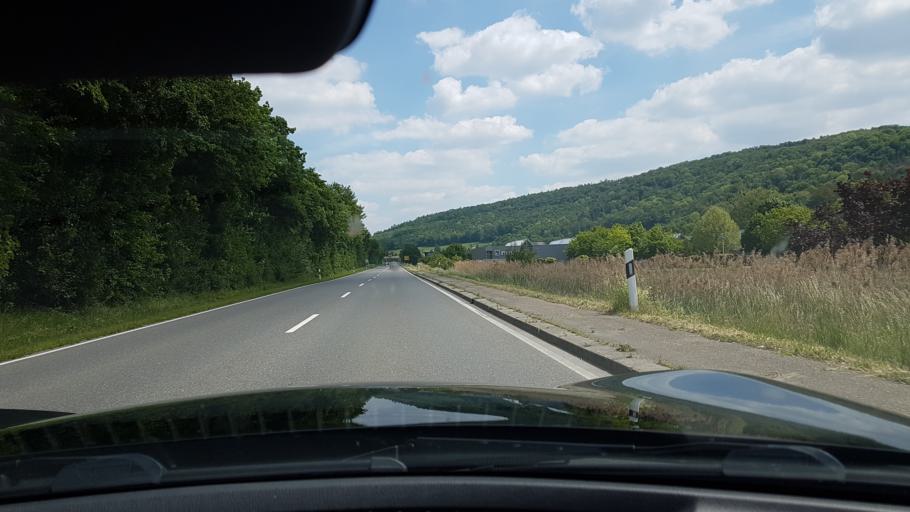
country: DE
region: Baden-Wuerttemberg
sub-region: Regierungsbezirk Stuttgart
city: Forchtenberg
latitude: 49.2925
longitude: 9.5652
